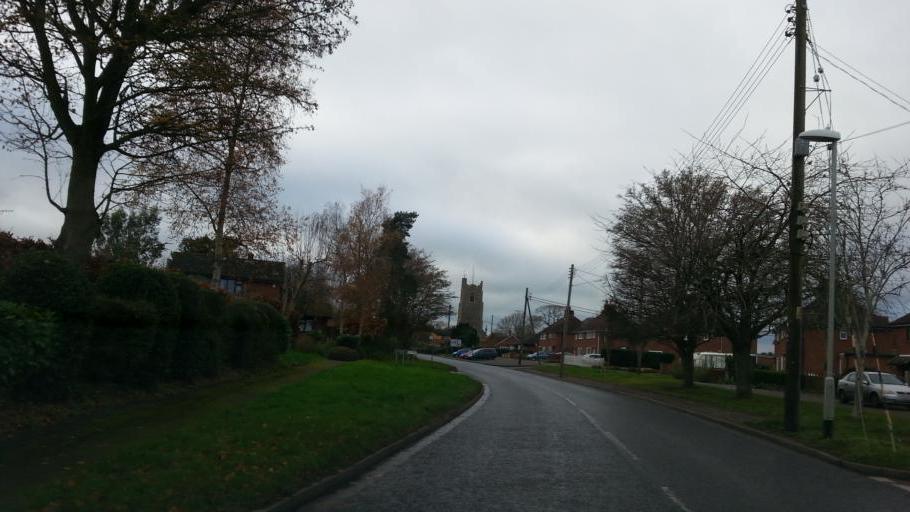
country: GB
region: England
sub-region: Norfolk
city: Harleston
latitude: 52.3192
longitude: 1.2772
